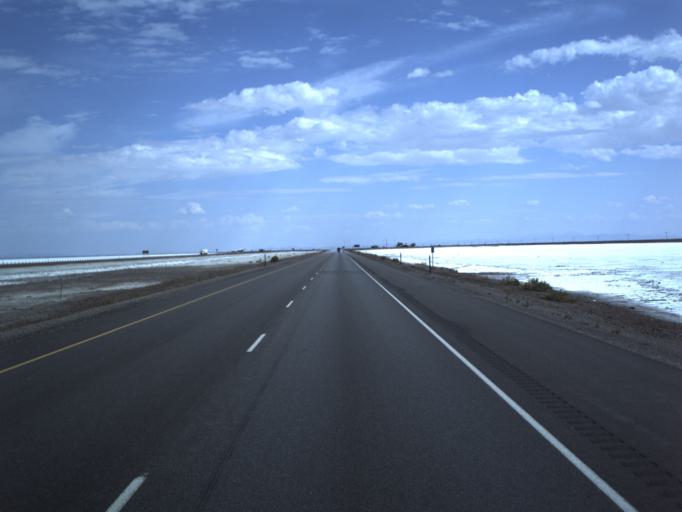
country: US
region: Utah
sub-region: Tooele County
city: Wendover
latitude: 40.7390
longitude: -113.8761
